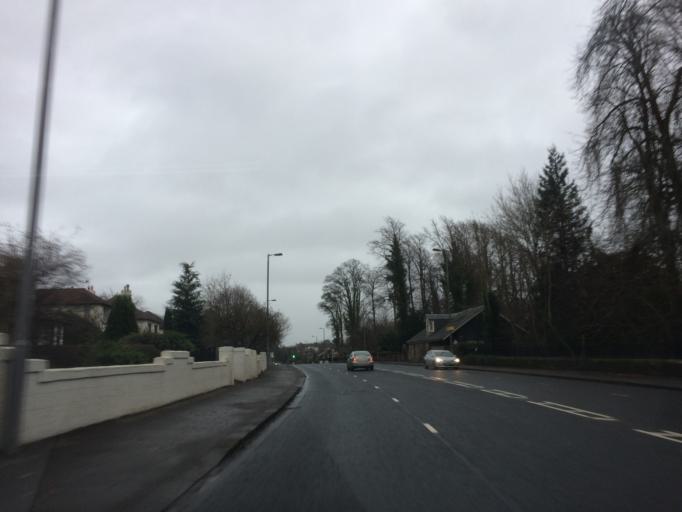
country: GB
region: Scotland
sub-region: East Renfrewshire
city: Giffnock
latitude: 55.7982
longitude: -4.3129
